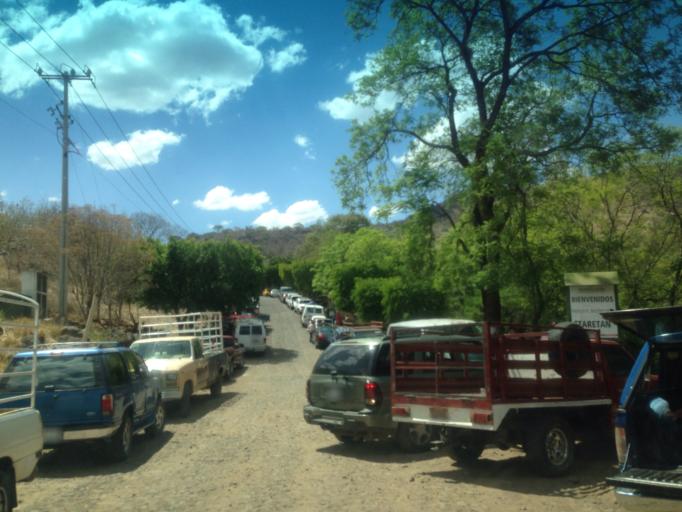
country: MX
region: Jalisco
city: Atotonilco el Alto
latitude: 20.5666
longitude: -102.5150
